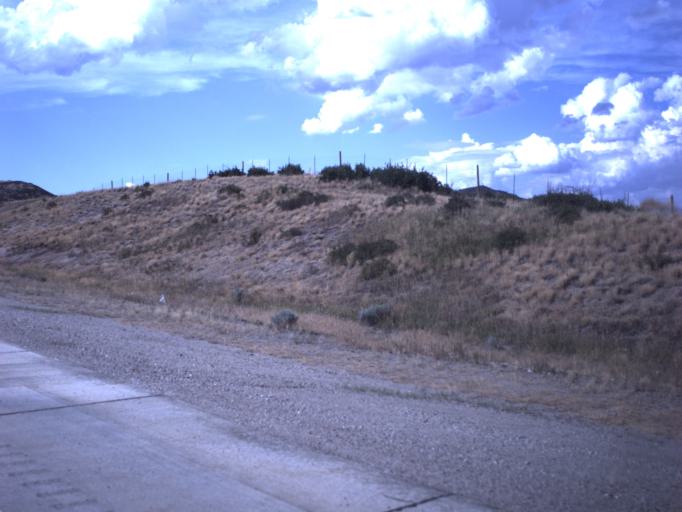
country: US
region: Utah
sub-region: Summit County
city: Park City
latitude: 40.6379
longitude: -111.4509
